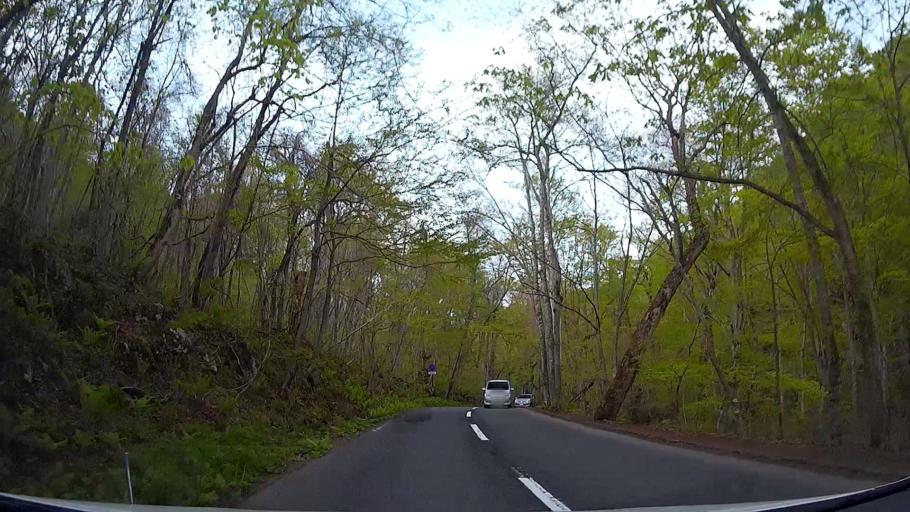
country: JP
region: Aomori
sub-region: Aomori Shi
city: Furudate
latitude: 40.5224
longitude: 140.9730
